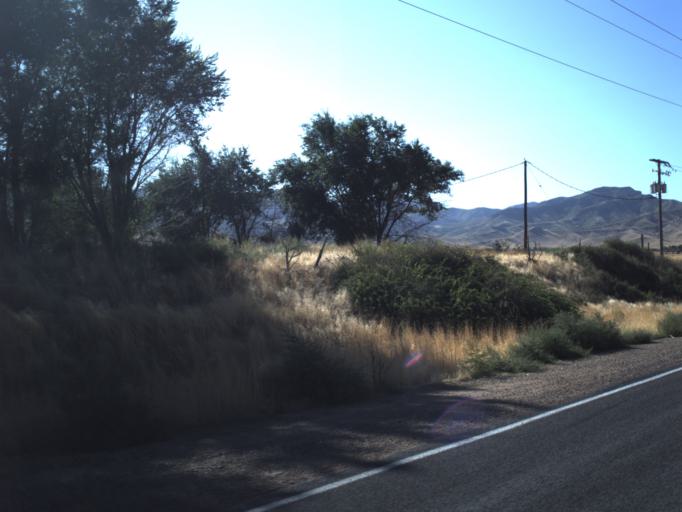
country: US
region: Utah
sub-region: Millard County
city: Delta
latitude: 39.3955
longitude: -112.3355
